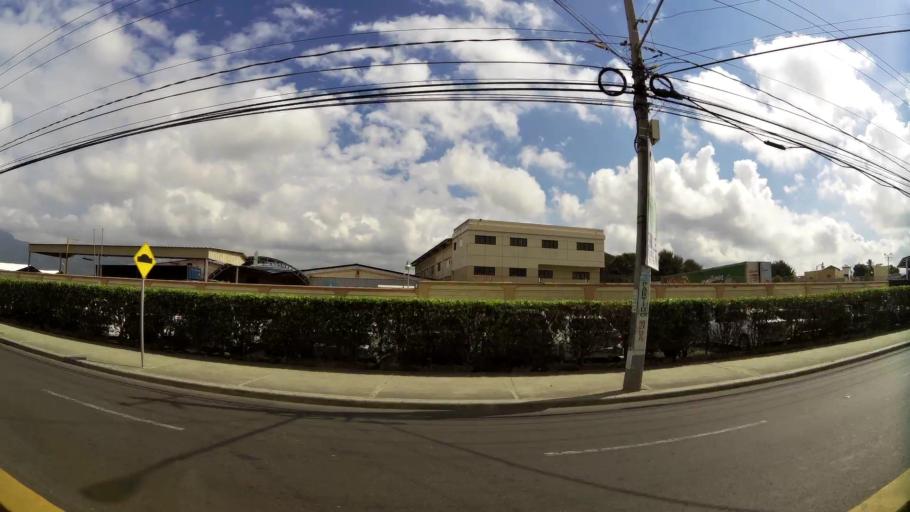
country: DO
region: Santiago
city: Santiago de los Caballeros
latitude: 19.4867
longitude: -70.7132
